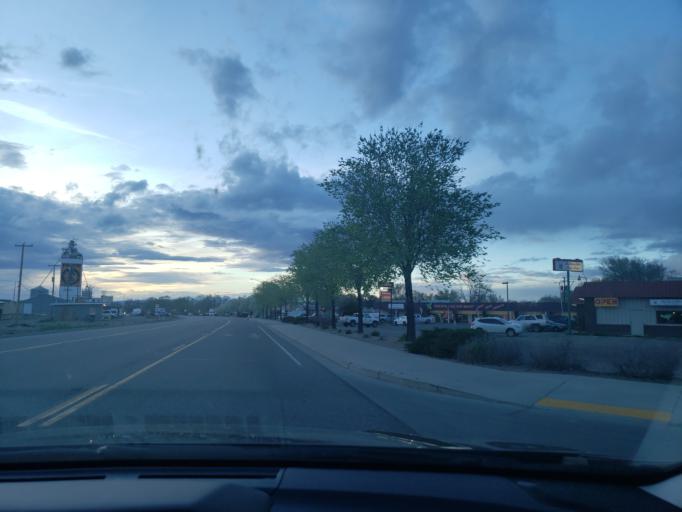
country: US
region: Colorado
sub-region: Mesa County
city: Fruita
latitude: 39.1538
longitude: -108.7293
